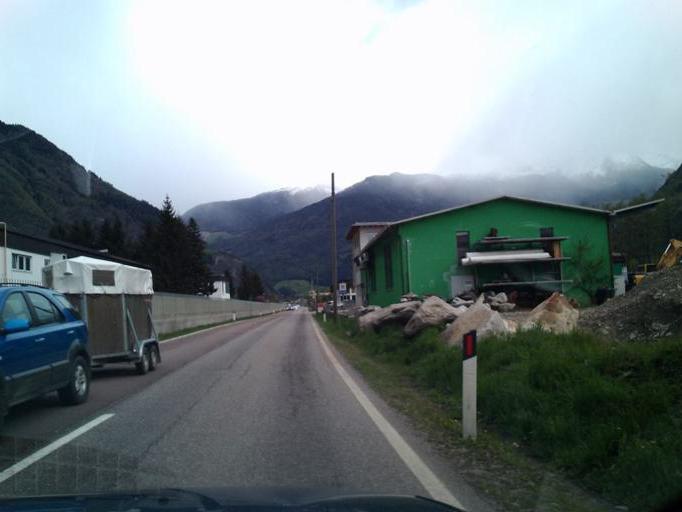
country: IT
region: Trentino-Alto Adige
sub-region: Bolzano
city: Molini di Tures
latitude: 46.8897
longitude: 11.9448
